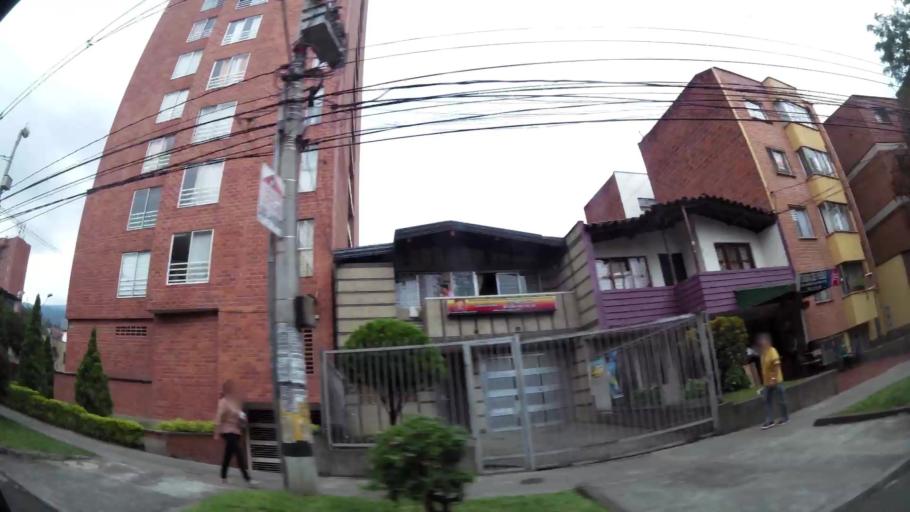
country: CO
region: Antioquia
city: Medellin
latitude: 6.2665
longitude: -75.5945
